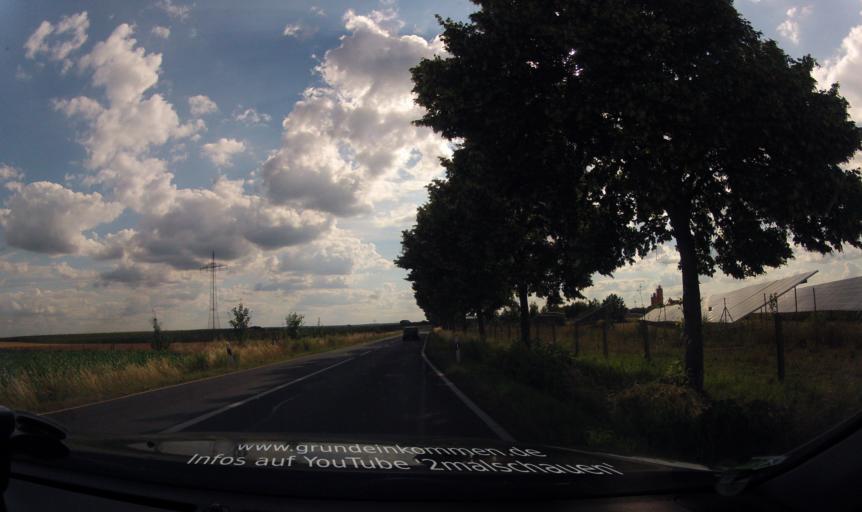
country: DE
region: Saxony
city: Hohburg
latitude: 51.3819
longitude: 12.7852
